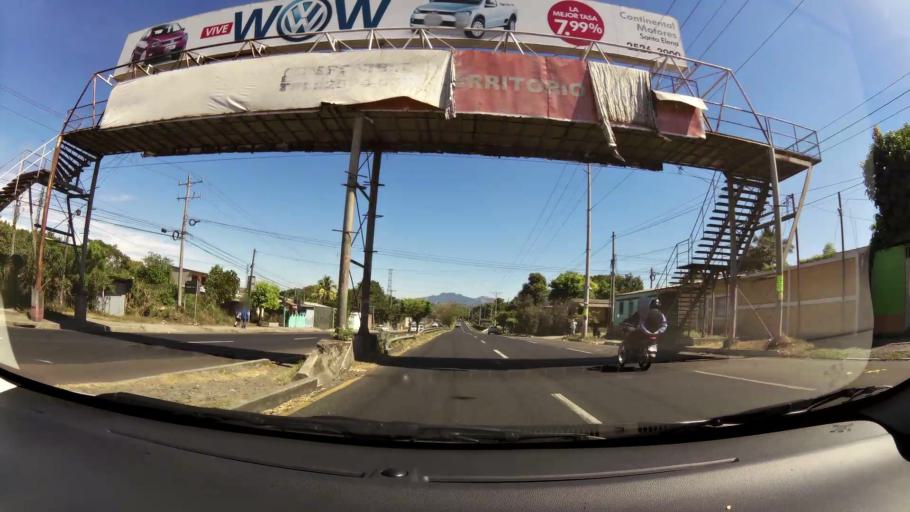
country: SV
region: La Libertad
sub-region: Distrito de Quezaltepeque
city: Quezaltepeque
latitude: 13.8240
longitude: -89.2727
